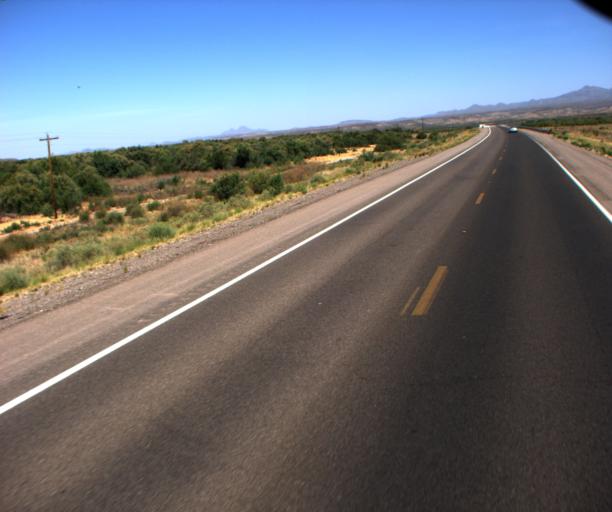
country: US
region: Arizona
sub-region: Graham County
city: Bylas
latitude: 33.1593
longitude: -110.1314
